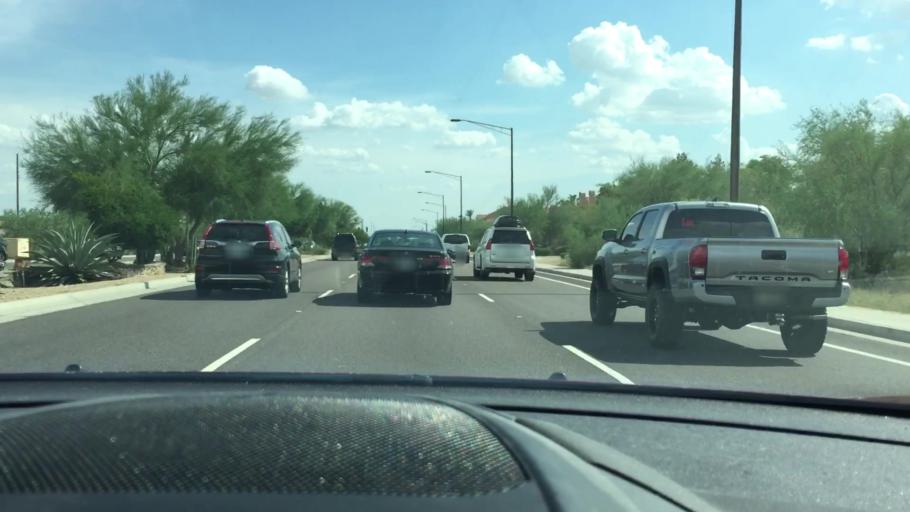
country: US
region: Arizona
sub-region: Maricopa County
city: Paradise Valley
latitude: 33.6447
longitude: -111.9257
